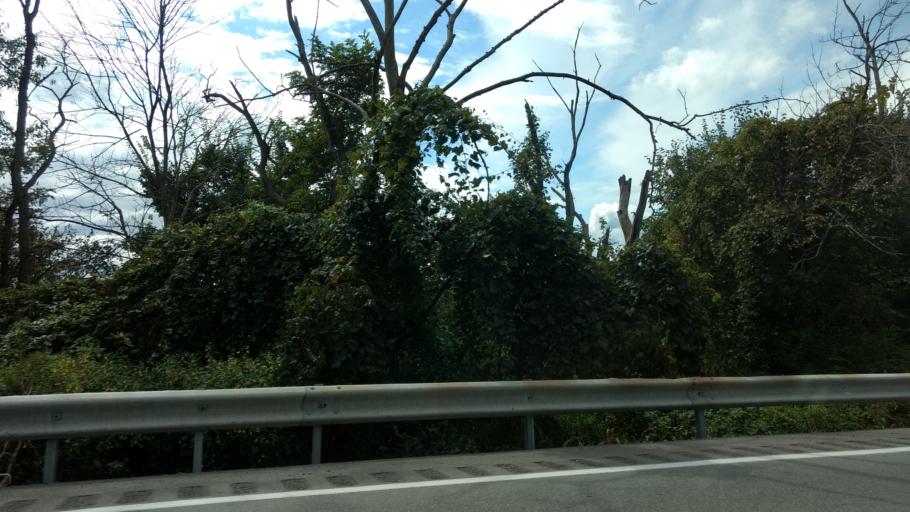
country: US
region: Pennsylvania
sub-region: Washington County
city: Wickerham Manor-Fisher
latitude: 40.1798
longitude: -79.9155
